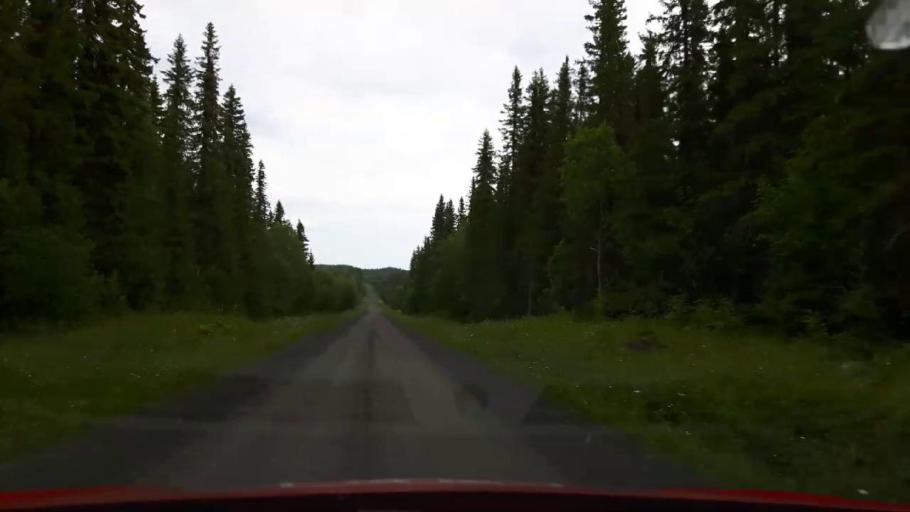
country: SE
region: Jaemtland
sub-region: OEstersunds Kommun
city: Lit
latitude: 63.3923
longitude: 15.2154
